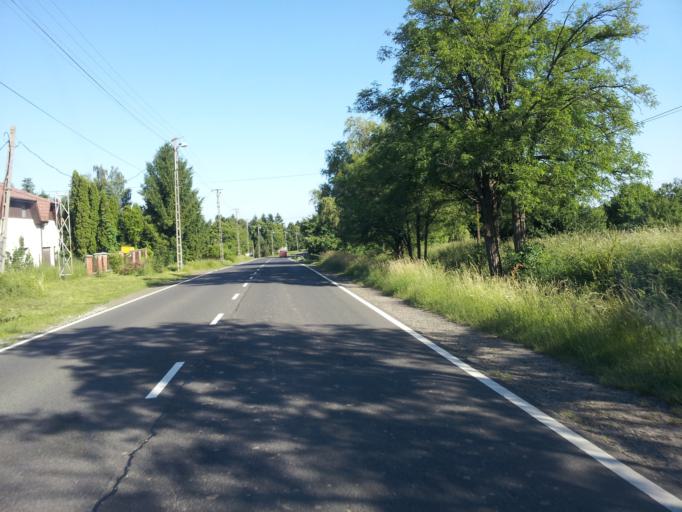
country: HU
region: Nograd
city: Nagyoroszi
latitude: 47.9952
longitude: 19.0995
